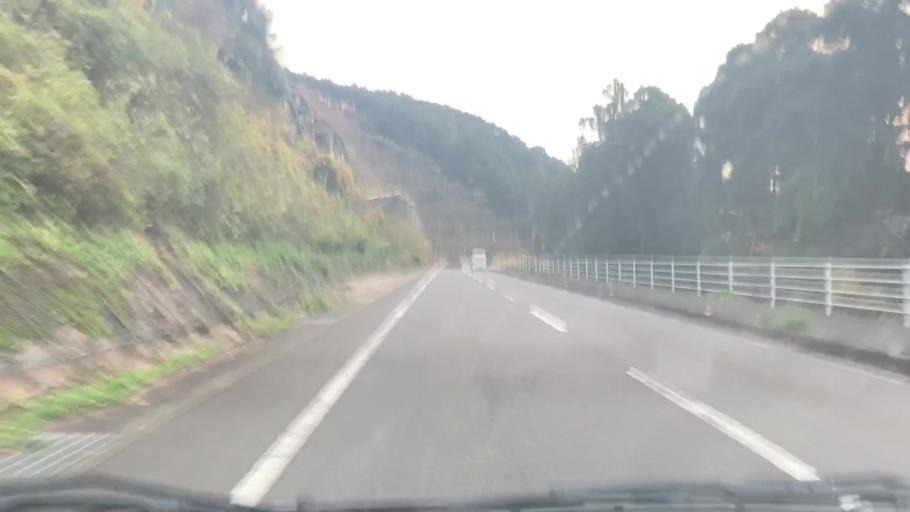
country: JP
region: Saga Prefecture
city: Kashima
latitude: 33.0431
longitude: 130.0717
